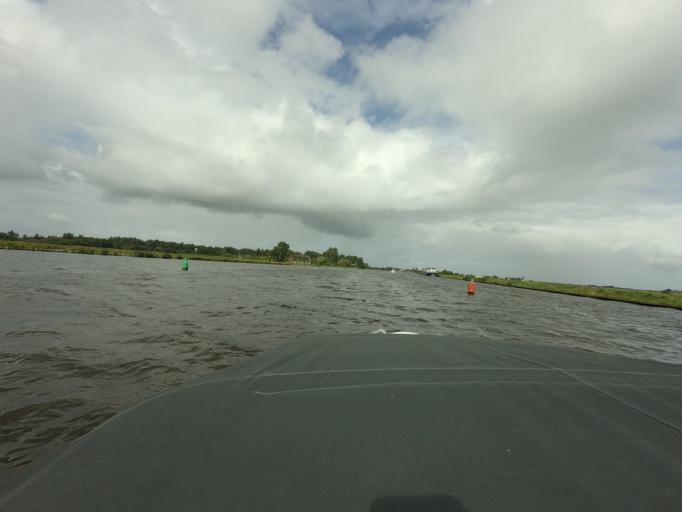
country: NL
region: Friesland
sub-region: Gemeente Boarnsterhim
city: Warten
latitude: 53.1364
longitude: 5.9172
